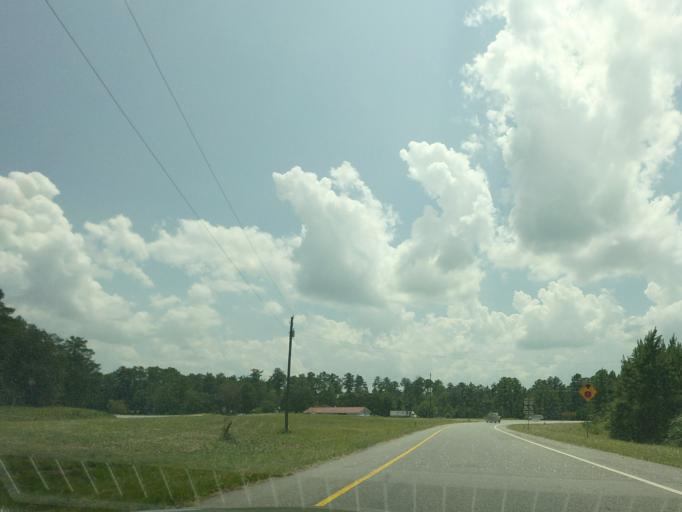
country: US
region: Georgia
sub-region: Bleckley County
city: Cochran
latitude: 32.3749
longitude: -83.3324
